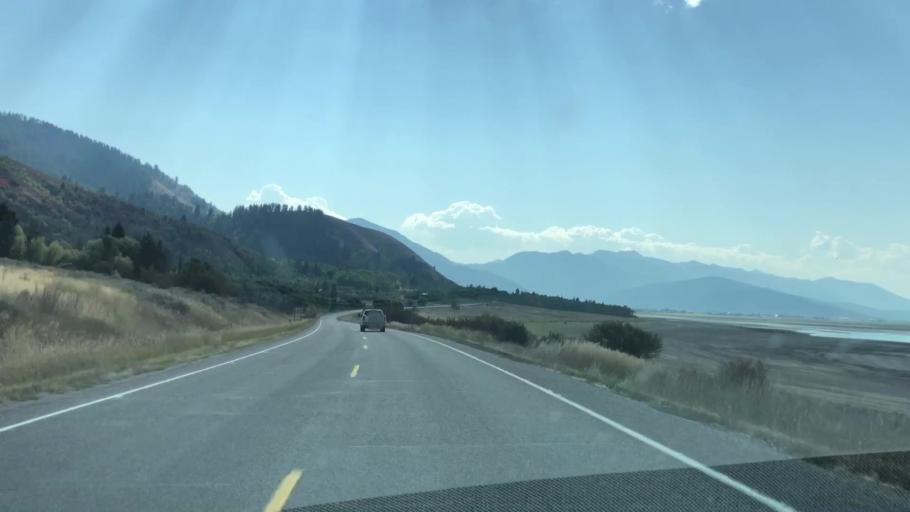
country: US
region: Wyoming
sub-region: Teton County
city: Hoback
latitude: 43.2189
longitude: -111.0701
